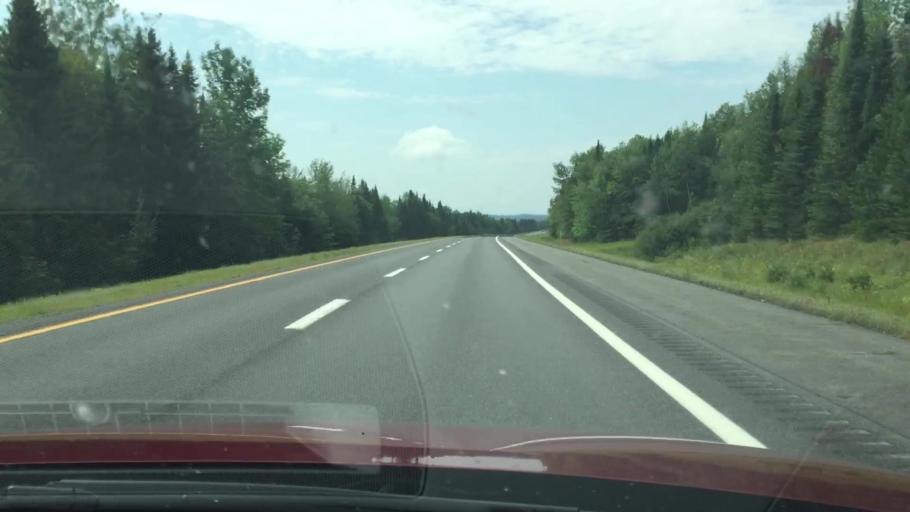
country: US
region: Maine
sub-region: Aroostook County
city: Hodgdon
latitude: 46.1206
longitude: -68.1175
